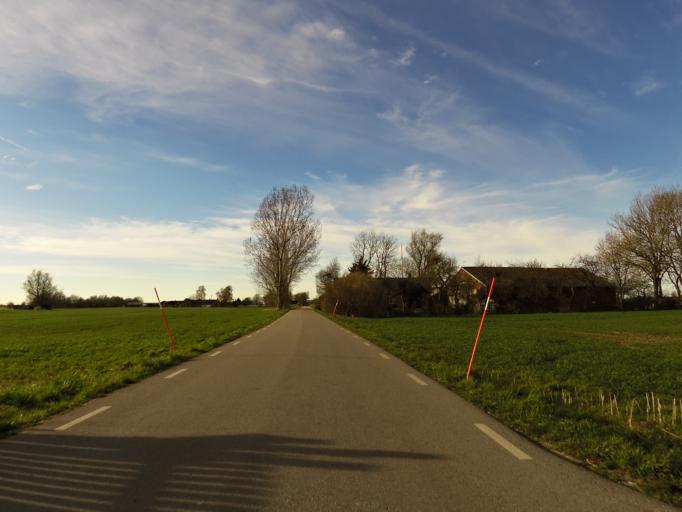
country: SE
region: Skane
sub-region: Kavlinge Kommun
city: Loddekopinge
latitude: 55.7452
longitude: 13.0668
